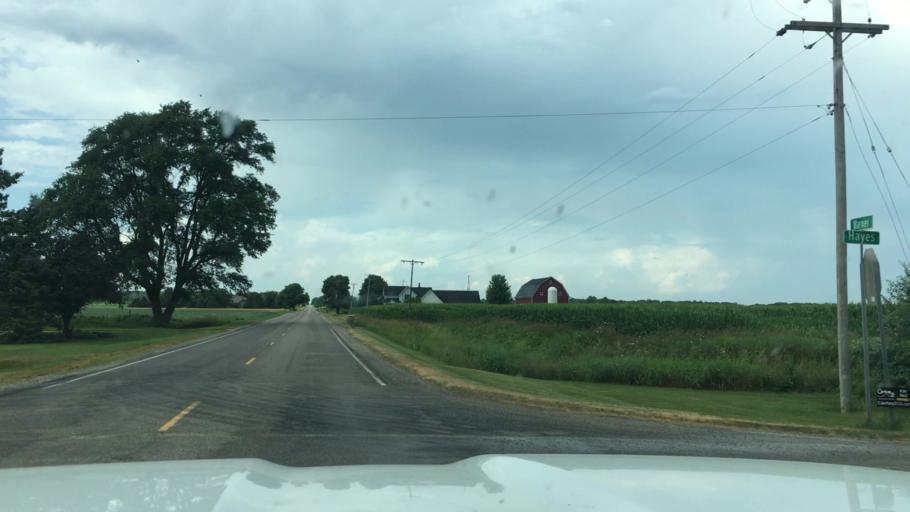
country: US
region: Michigan
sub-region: Montcalm County
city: Carson City
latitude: 43.2197
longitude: -84.7776
